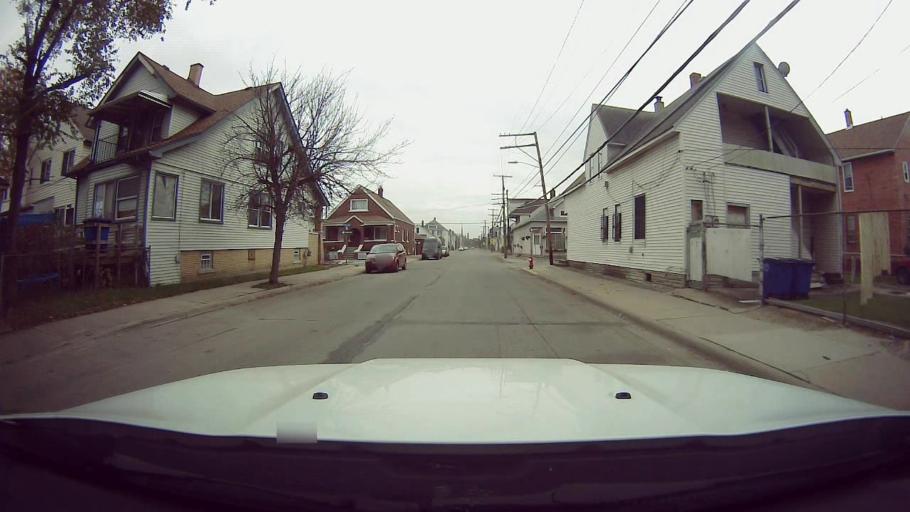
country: US
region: Michigan
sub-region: Wayne County
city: Hamtramck
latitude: 42.4024
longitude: -83.0648
